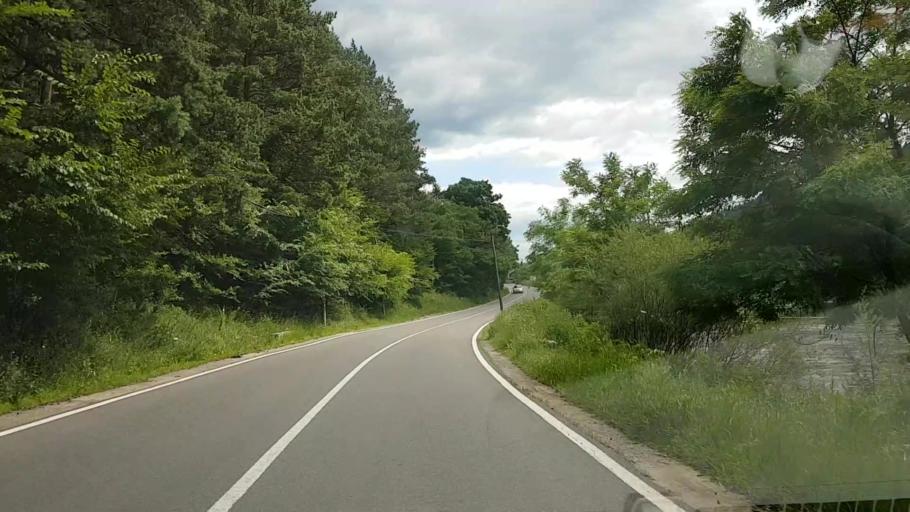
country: RO
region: Neamt
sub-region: Comuna Poiana Teiului
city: Poiana Teiului
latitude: 47.1215
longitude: 25.9100
